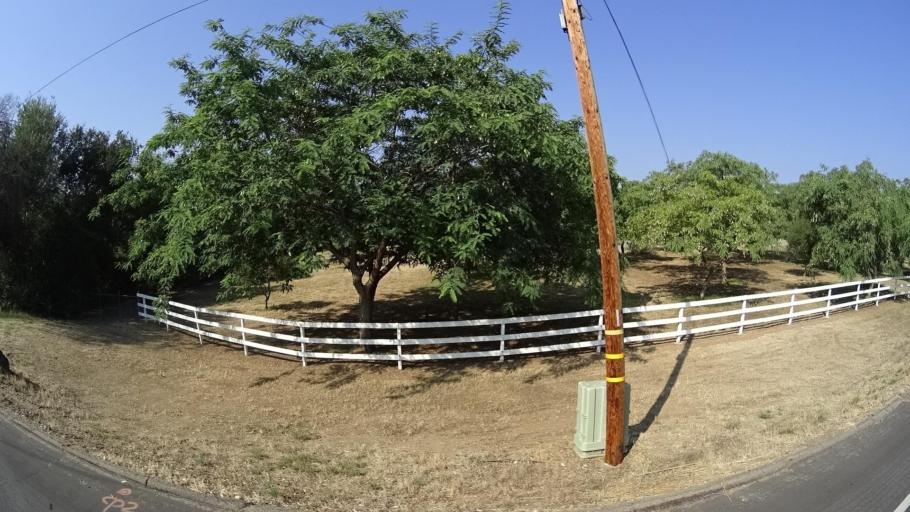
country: US
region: California
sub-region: San Diego County
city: Vista
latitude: 33.2334
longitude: -117.2501
